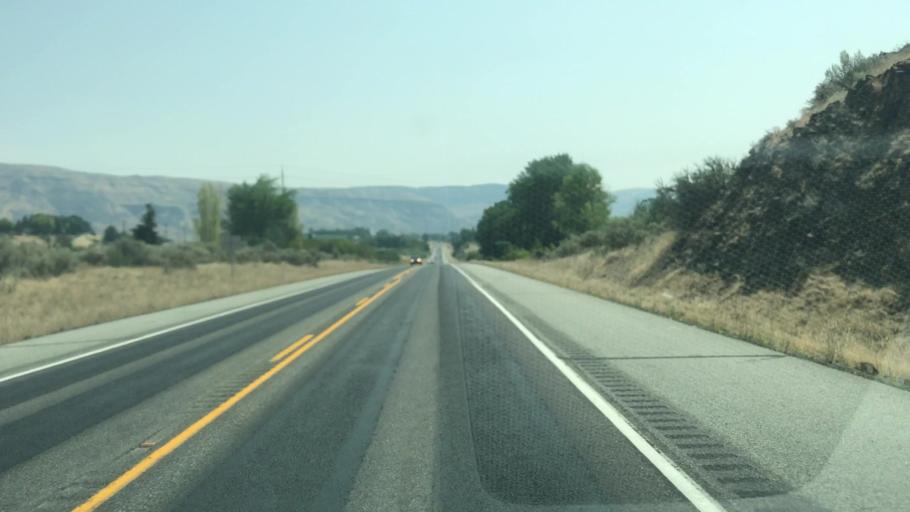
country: US
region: Washington
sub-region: Chelan County
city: South Wenatchee
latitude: 47.3759
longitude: -120.1843
